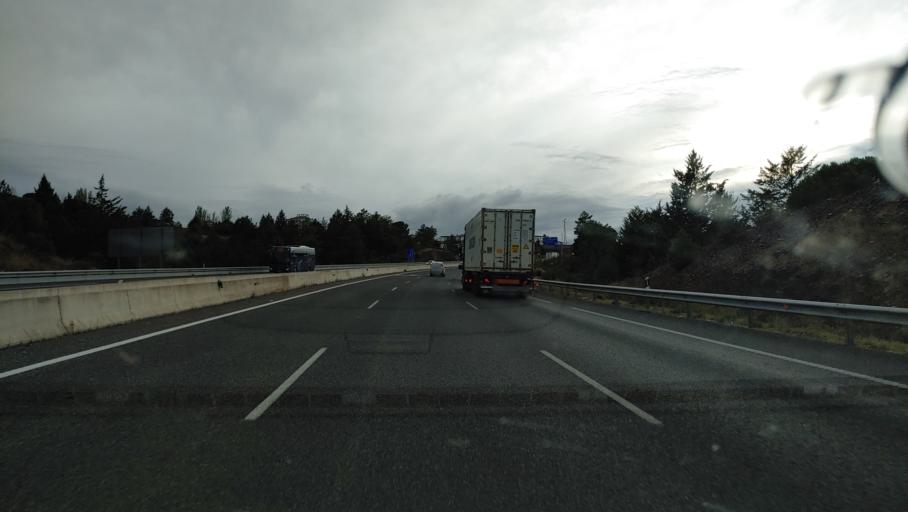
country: ES
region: Andalusia
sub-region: Provincia de Jaen
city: Santa Elena
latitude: 38.3474
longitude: -3.5339
